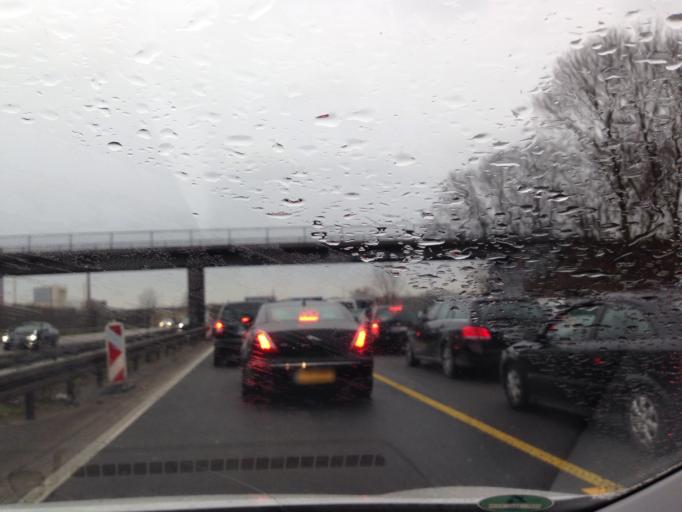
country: DE
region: North Rhine-Westphalia
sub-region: Regierungsbezirk Dusseldorf
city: Moers
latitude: 51.4373
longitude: 6.6850
